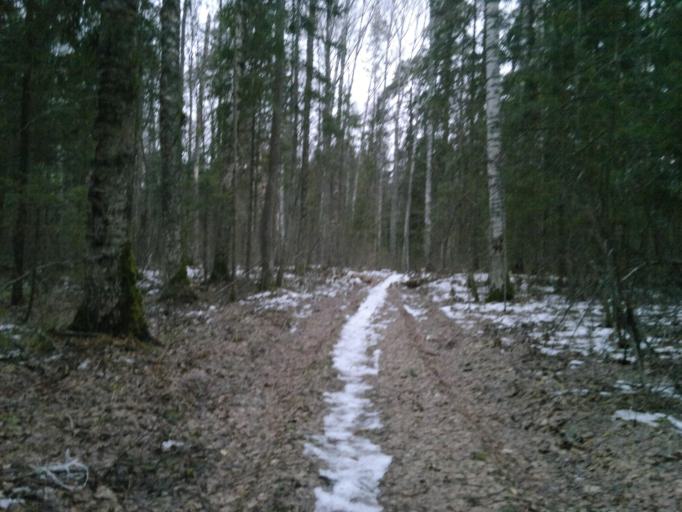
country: RU
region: Mariy-El
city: Yoshkar-Ola
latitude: 56.6051
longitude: 47.9556
